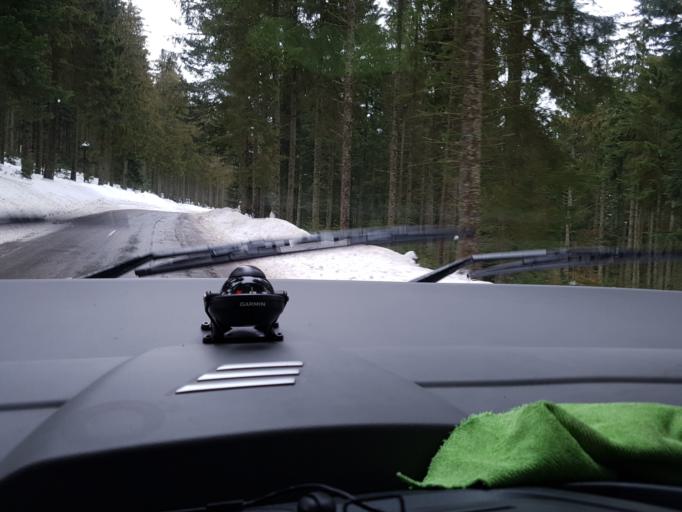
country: FR
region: Lorraine
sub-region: Departement des Vosges
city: Plainfaing
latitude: 48.1427
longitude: 7.0645
